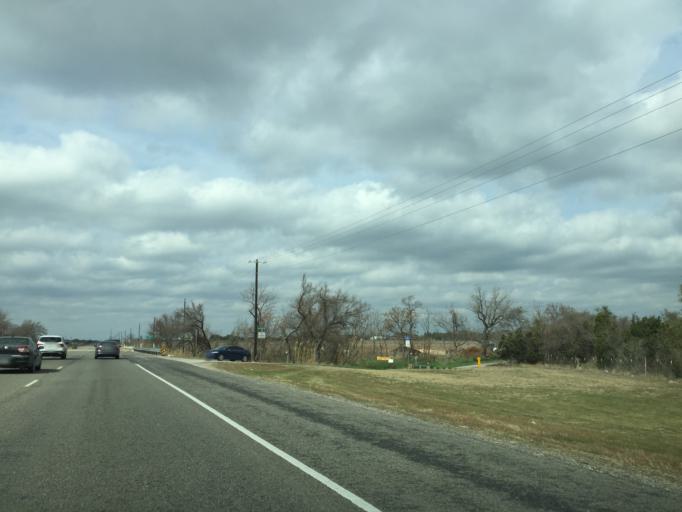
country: US
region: Texas
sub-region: Travis County
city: Briarcliff
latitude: 30.4655
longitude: -98.1667
